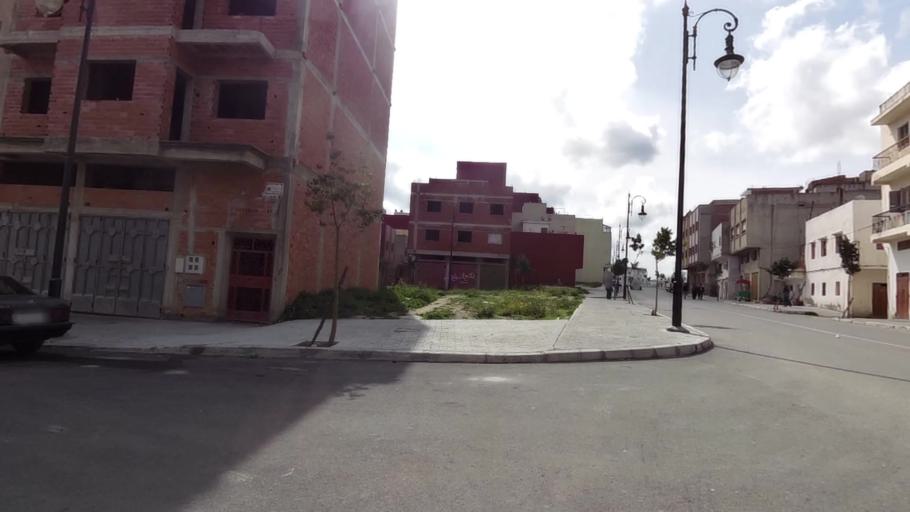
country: MA
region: Tanger-Tetouan
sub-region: Tanger-Assilah
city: Tangier
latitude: 35.7639
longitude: -5.7632
